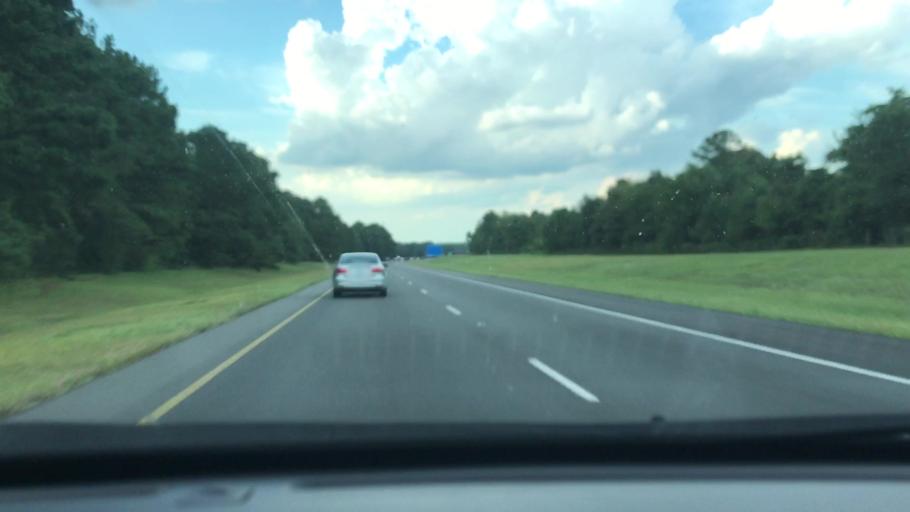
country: US
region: North Carolina
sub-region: Cumberland County
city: Eastover
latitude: 35.0721
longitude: -78.7912
